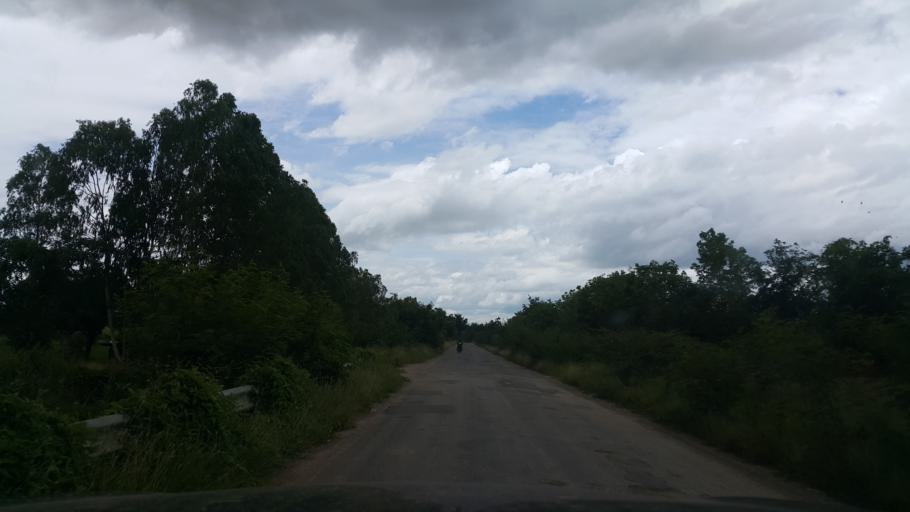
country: TH
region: Sukhothai
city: Ban Na
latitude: 17.0468
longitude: 99.7755
